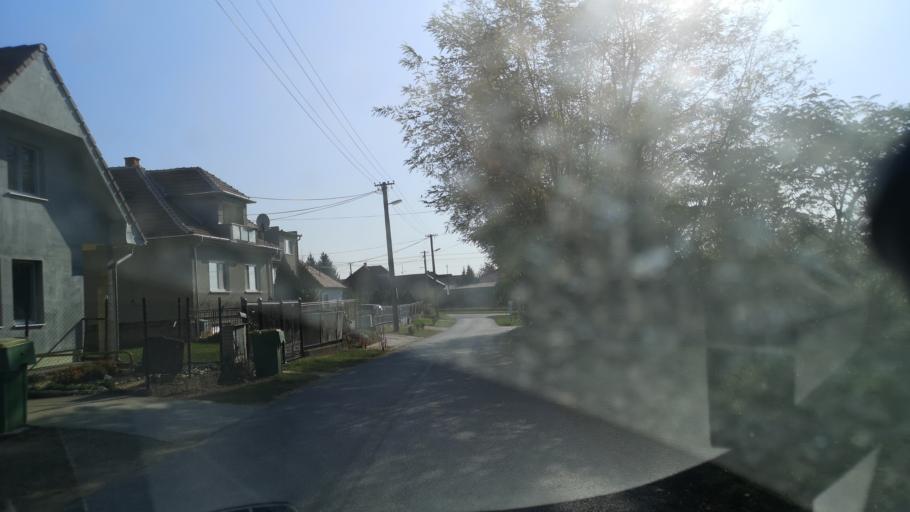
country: SK
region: Nitriansky
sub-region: Okres Nitra
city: Nitra
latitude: 48.3085
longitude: 17.9463
